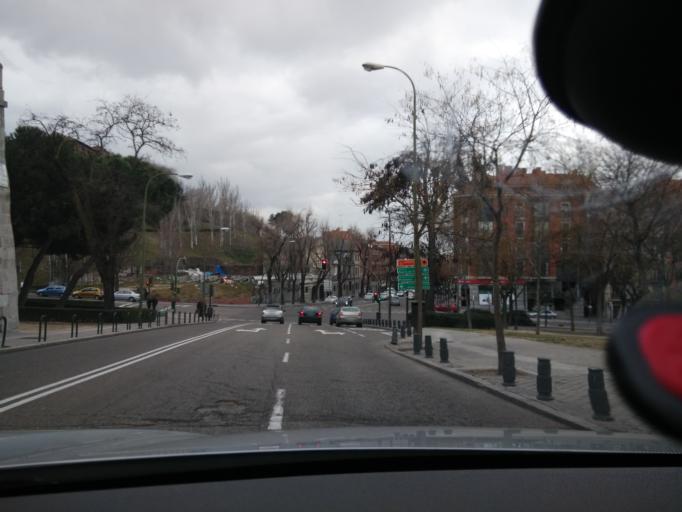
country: ES
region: Madrid
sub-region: Provincia de Madrid
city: Madrid
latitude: 40.4146
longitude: -3.7168
